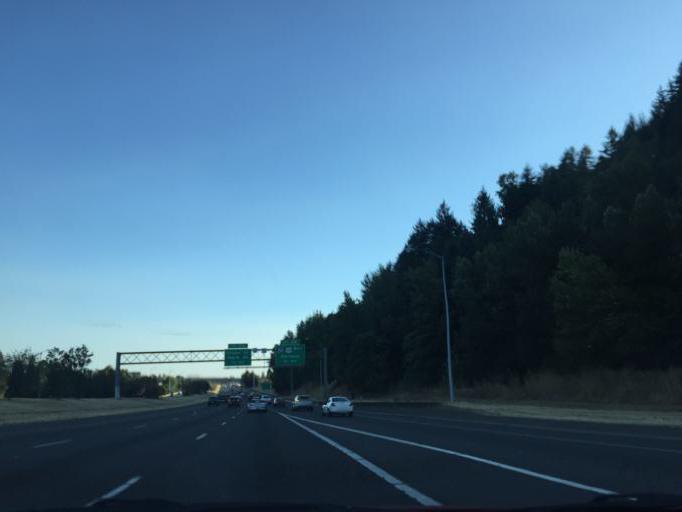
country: US
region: Oregon
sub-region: Multnomah County
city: Lents
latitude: 45.5417
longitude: -122.5625
